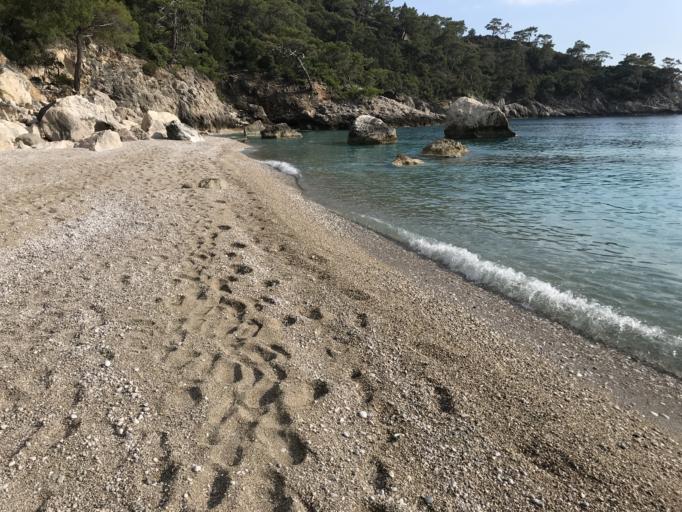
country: TR
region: Mugla
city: OEluedeniz
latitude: 36.4403
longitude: 29.1314
